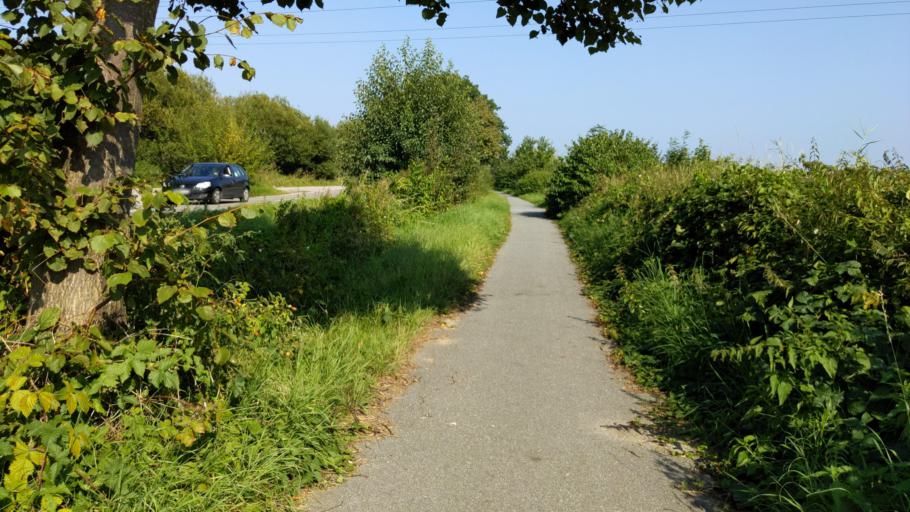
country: DE
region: Schleswig-Holstein
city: Badendorf
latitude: 53.8731
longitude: 10.6021
